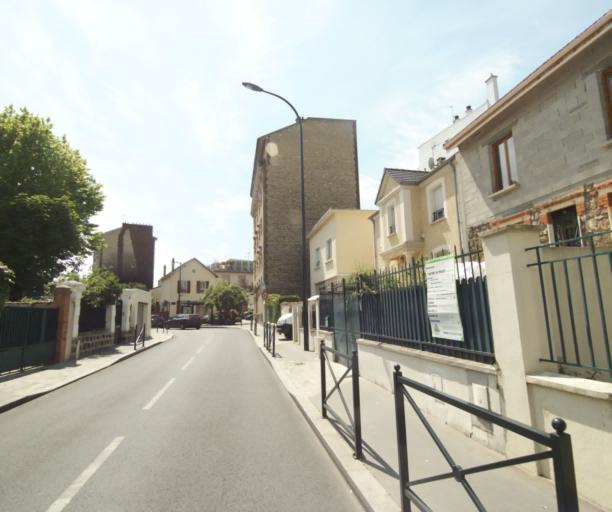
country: FR
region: Ile-de-France
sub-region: Departement des Hauts-de-Seine
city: Bois-Colombes
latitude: 48.9108
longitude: 2.2648
